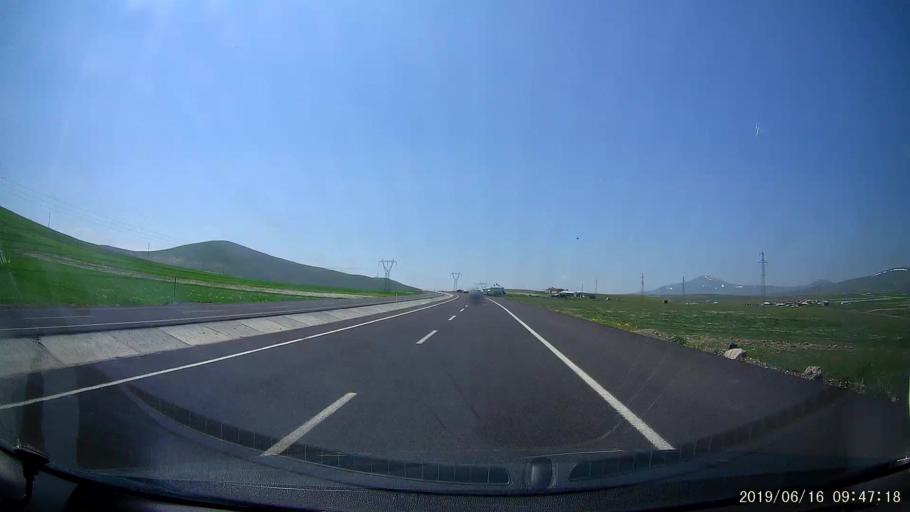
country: TR
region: Kars
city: Digor
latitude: 40.4498
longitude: 43.3426
